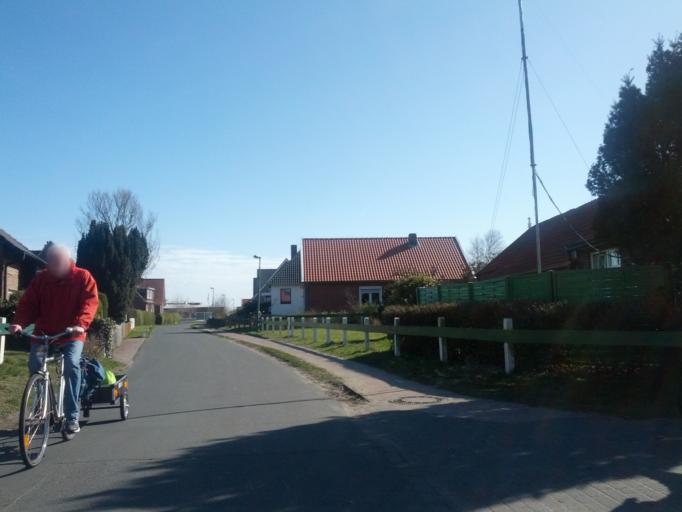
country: DE
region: Lower Saxony
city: Langeoog
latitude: 53.7433
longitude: 7.4854
